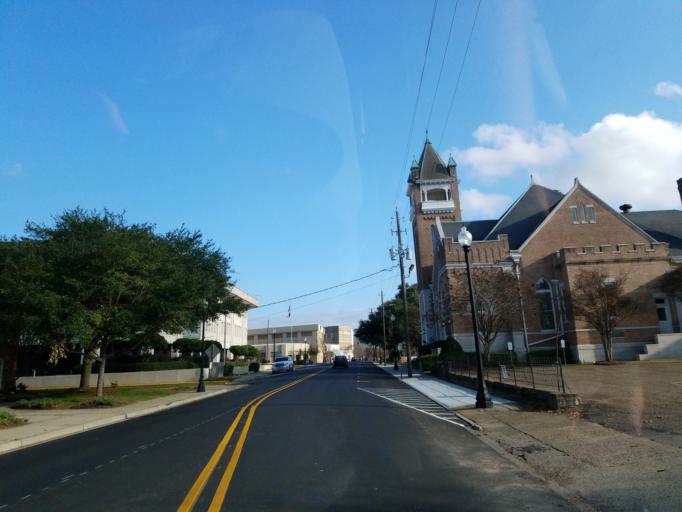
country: US
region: Mississippi
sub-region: Forrest County
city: Hattiesburg
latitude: 31.3283
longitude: -89.2929
